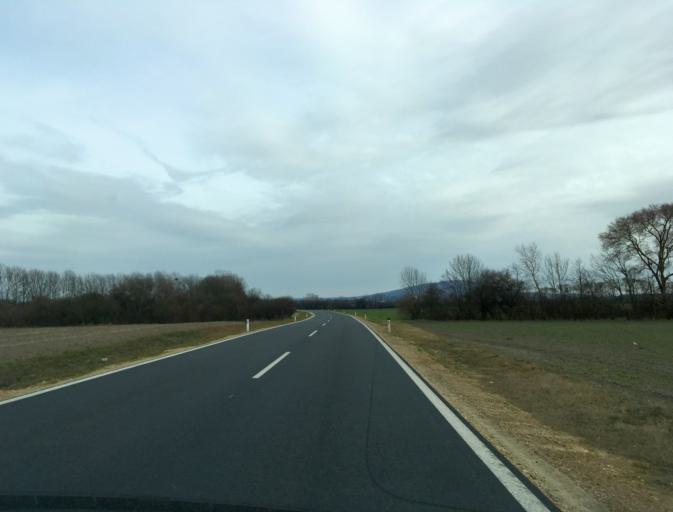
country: AT
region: Lower Austria
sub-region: Politischer Bezirk Ganserndorf
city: Lassee
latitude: 48.2223
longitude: 16.8759
